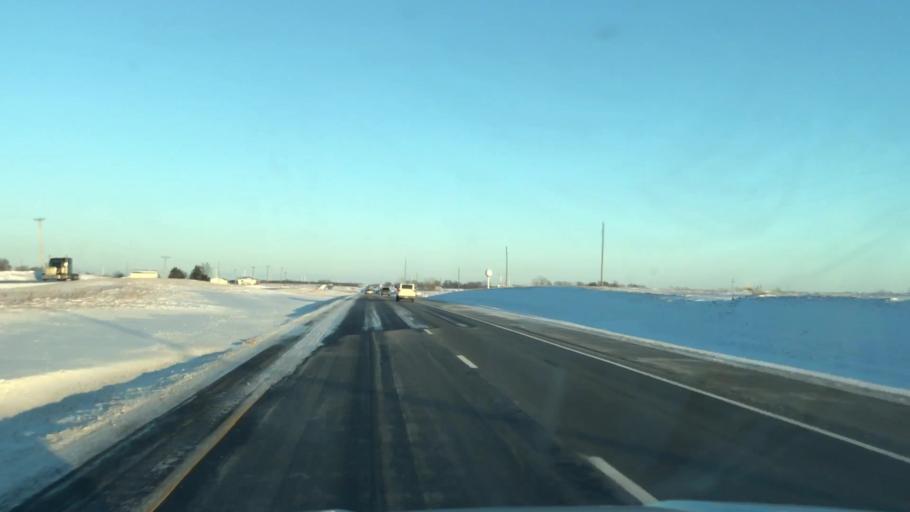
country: US
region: Missouri
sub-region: Clinton County
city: Gower
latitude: 39.7620
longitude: -94.5230
